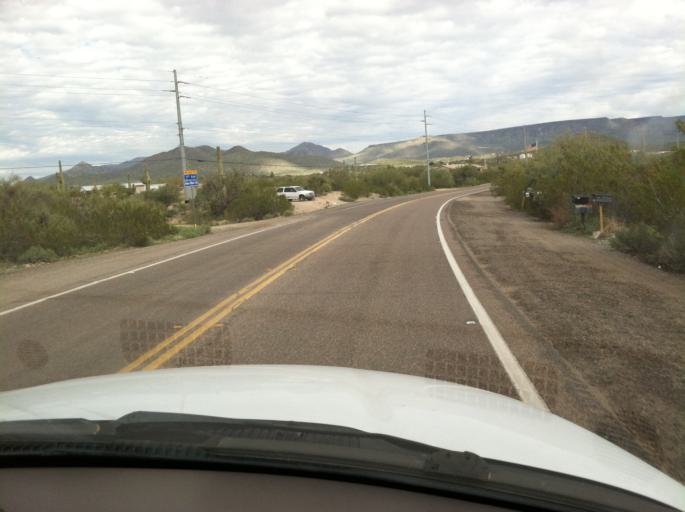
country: US
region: Arizona
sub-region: Maricopa County
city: New River
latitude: 33.9207
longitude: -112.1273
